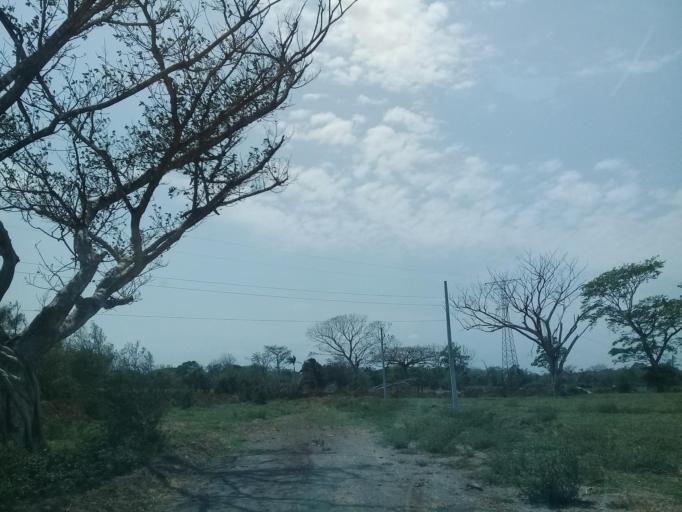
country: MX
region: Veracruz
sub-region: Veracruz
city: Delfino Victoria (Santa Fe)
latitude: 19.1734
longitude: -96.2817
